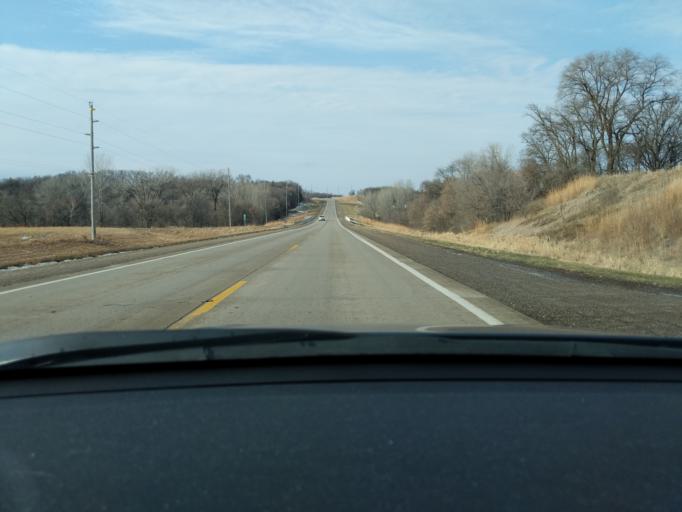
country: US
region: Minnesota
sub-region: Yellow Medicine County
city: Granite Falls
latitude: 44.7912
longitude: -95.4512
